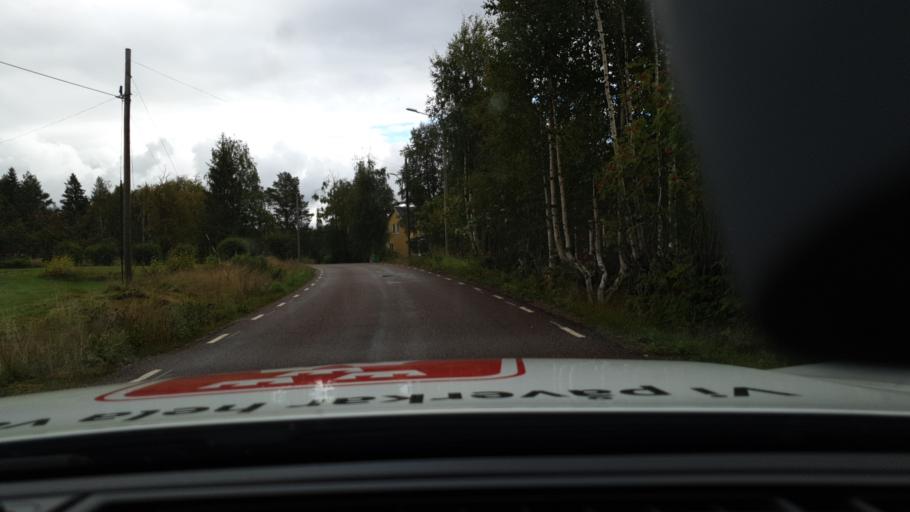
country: SE
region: Norrbotten
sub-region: Gallivare Kommun
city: Gaellivare
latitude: 66.9287
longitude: 21.5499
